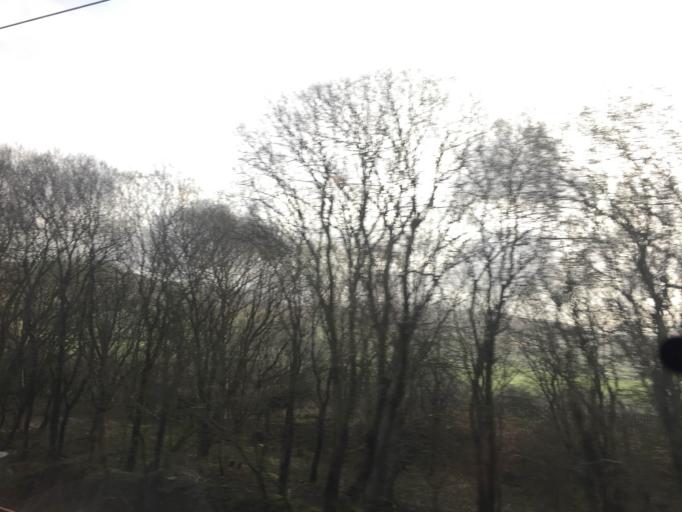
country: GB
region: England
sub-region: Cumbria
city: Sedbergh
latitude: 54.3668
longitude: -2.5864
